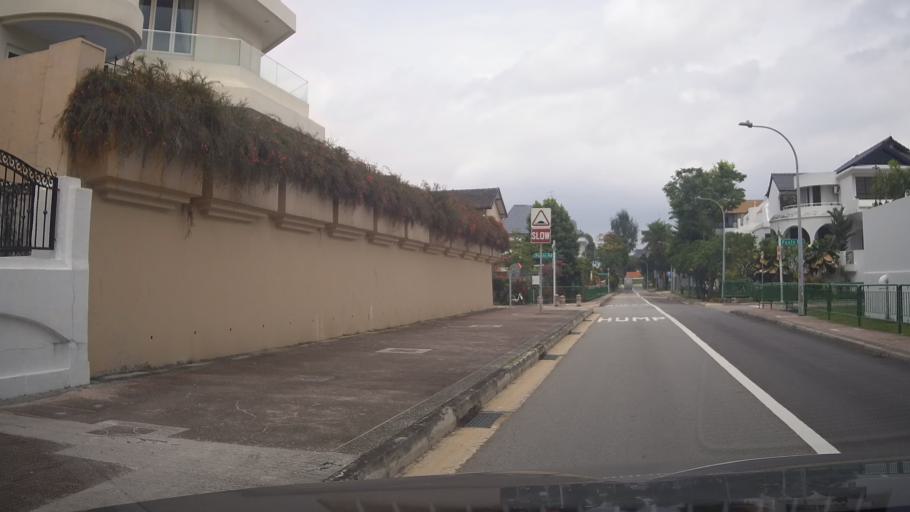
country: SG
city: Singapore
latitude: 1.3068
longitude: 103.8929
